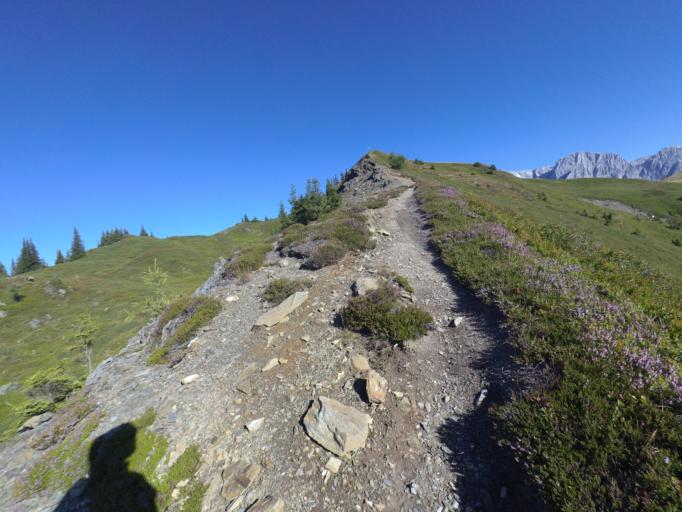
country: AT
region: Salzburg
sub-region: Politischer Bezirk Sankt Johann im Pongau
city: Goldegg
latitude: 47.3638
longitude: 13.0705
